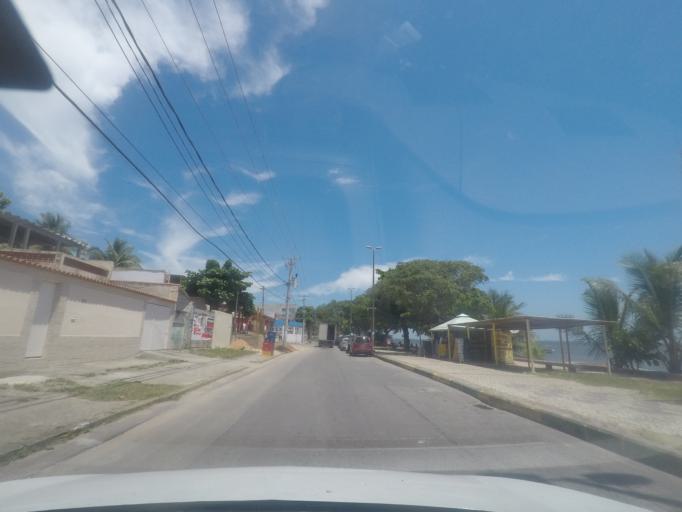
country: BR
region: Rio de Janeiro
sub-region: Itaguai
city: Itaguai
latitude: -22.9874
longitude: -43.6921
